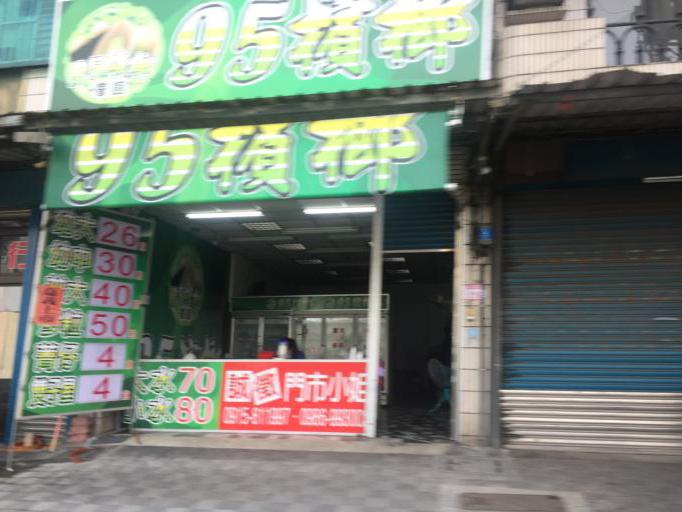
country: TW
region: Taiwan
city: Daxi
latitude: 24.8657
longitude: 121.2102
